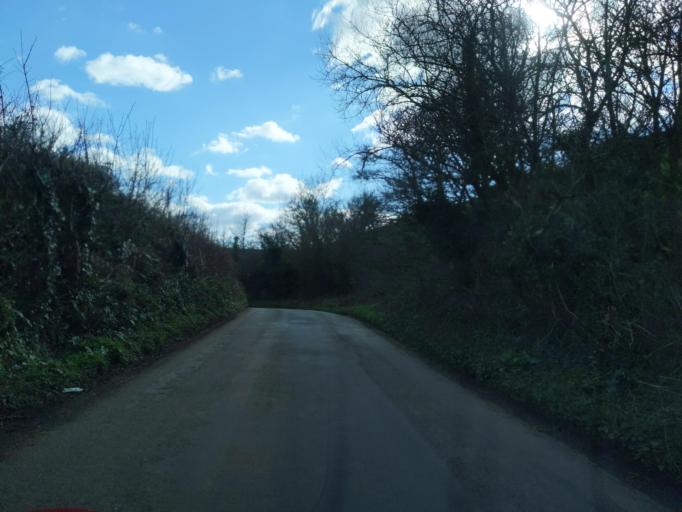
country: GB
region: England
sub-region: Devon
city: Salcombe
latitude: 50.2554
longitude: -3.7046
